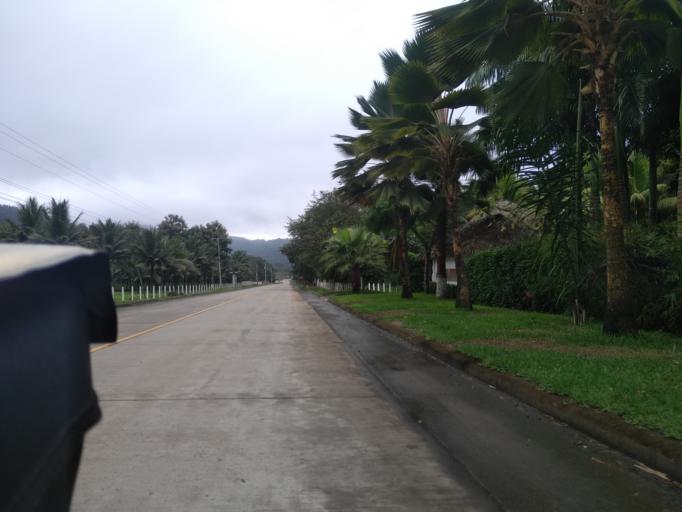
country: EC
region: Manabi
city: Jipijapa
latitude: -1.6659
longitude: -80.8122
